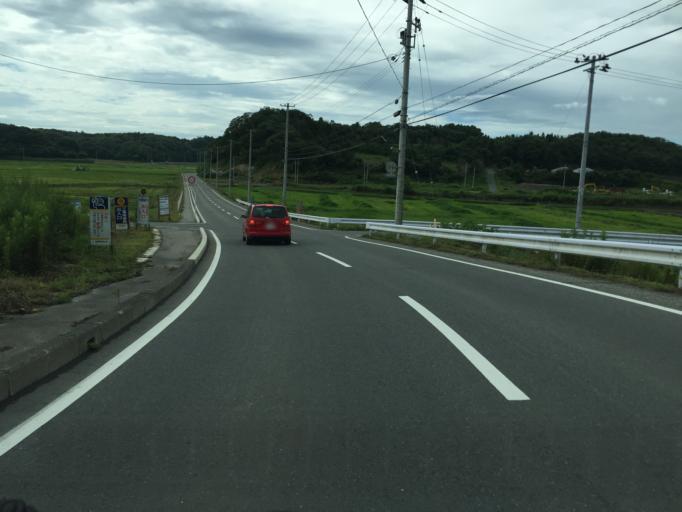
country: JP
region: Fukushima
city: Namie
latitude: 37.7583
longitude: 140.9926
